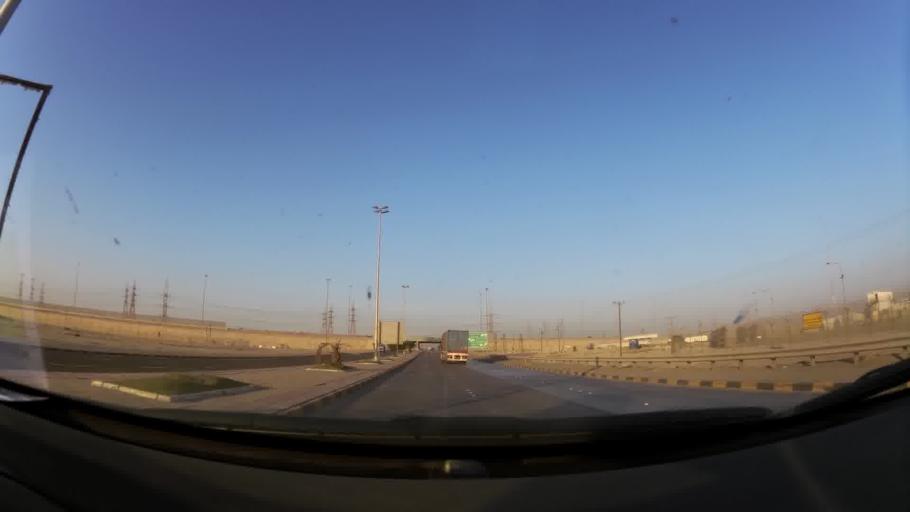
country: KW
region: Al Ahmadi
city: Al Fahahil
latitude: 29.0456
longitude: 48.1167
